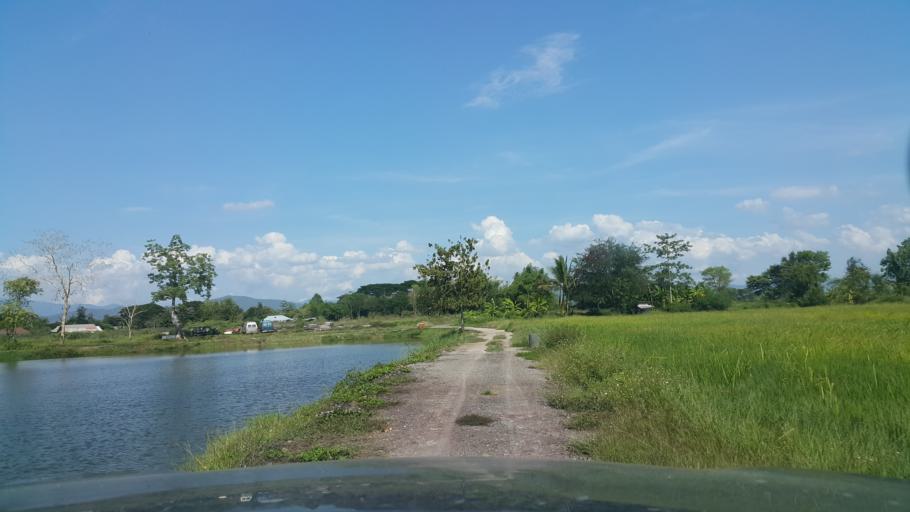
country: TH
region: Chiang Mai
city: San Kamphaeng
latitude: 18.8049
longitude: 99.1193
